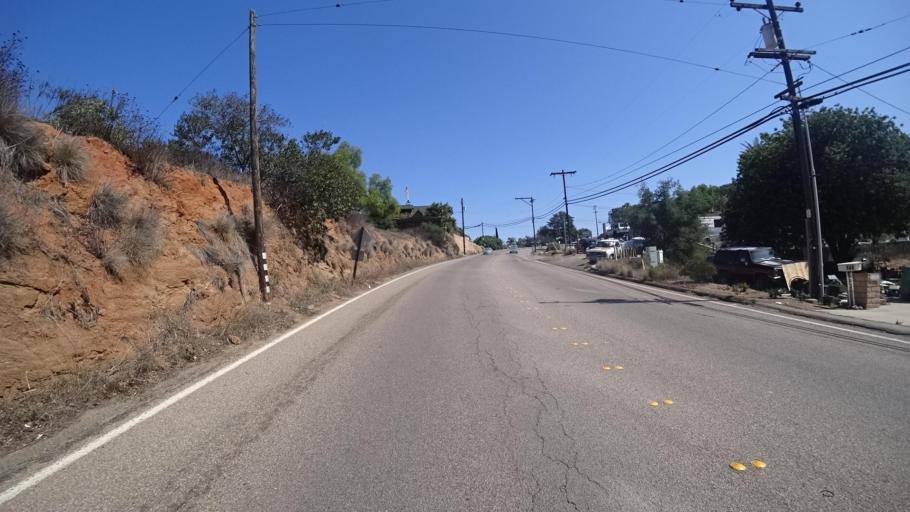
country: US
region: California
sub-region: San Diego County
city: Crest
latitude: 32.8151
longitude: -116.8636
